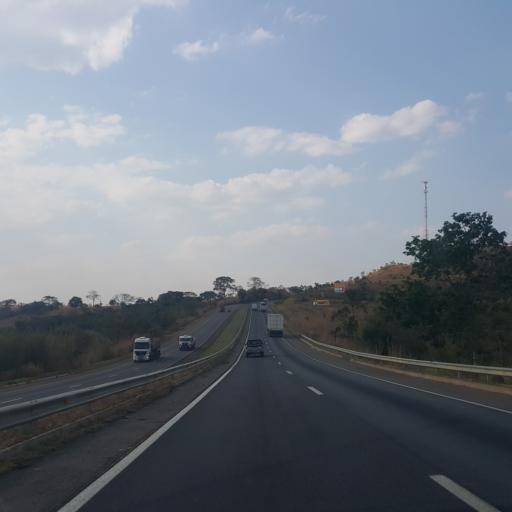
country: BR
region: Goias
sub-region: Abadiania
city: Abadiania
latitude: -16.1033
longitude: -48.5238
